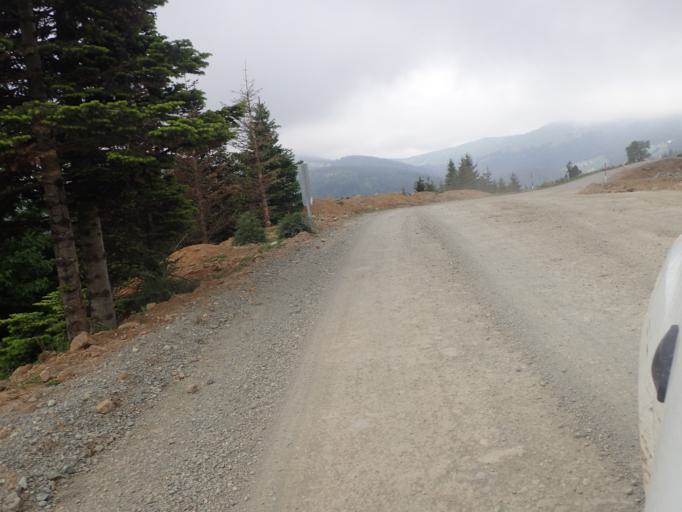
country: TR
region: Ordu
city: Topcam
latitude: 40.6595
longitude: 37.9420
